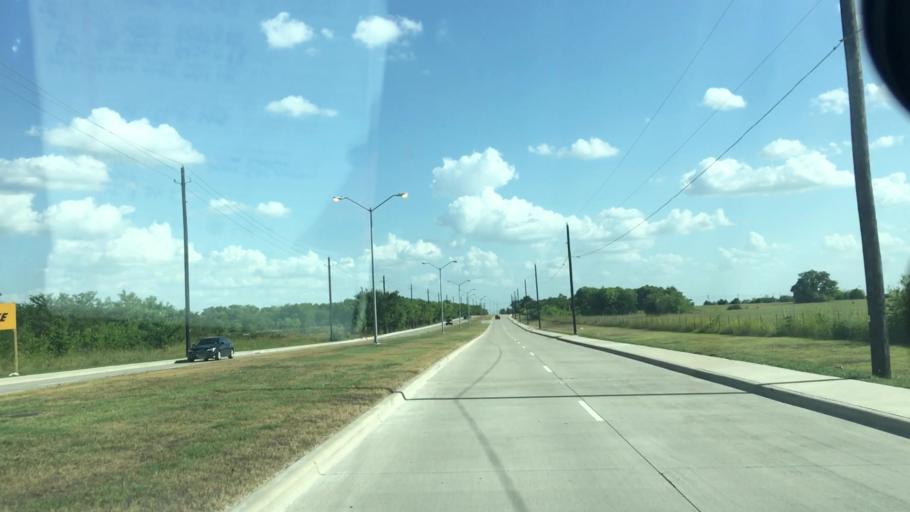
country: US
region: Texas
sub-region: Dallas County
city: Lancaster
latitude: 32.6257
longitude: -96.7529
